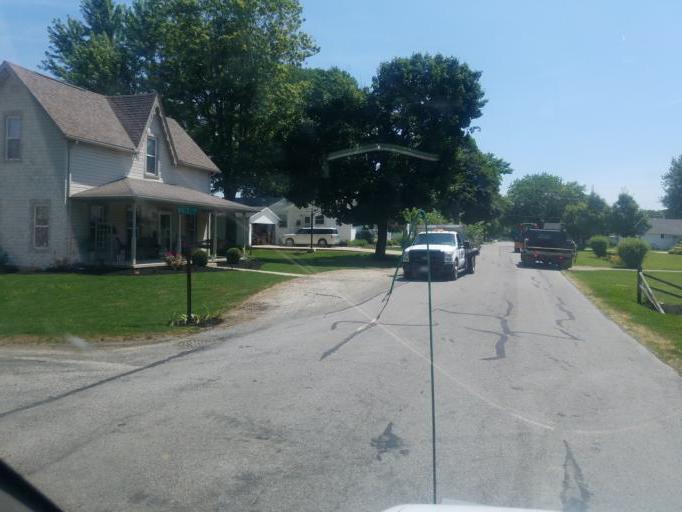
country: US
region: Ohio
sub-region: Logan County
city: West Liberty
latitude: 40.2562
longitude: -83.7531
